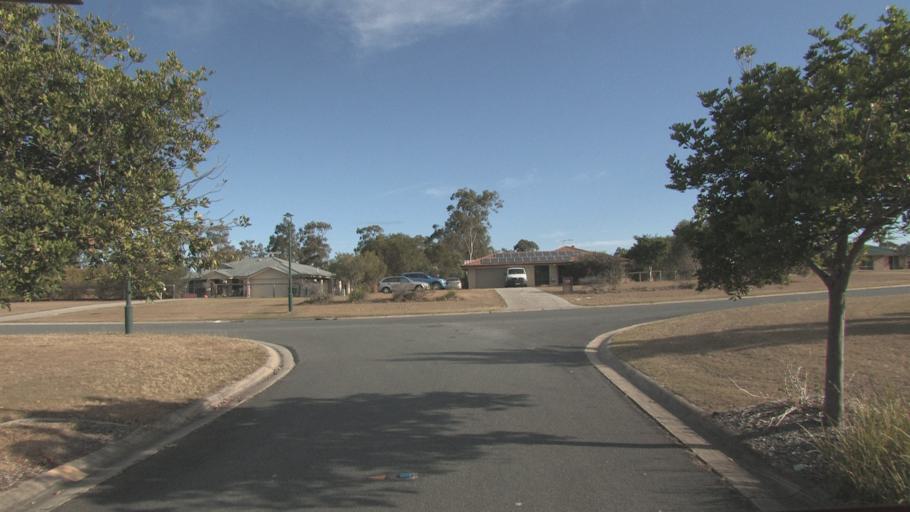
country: AU
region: Queensland
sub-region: Logan
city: North Maclean
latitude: -27.7993
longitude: 152.9617
